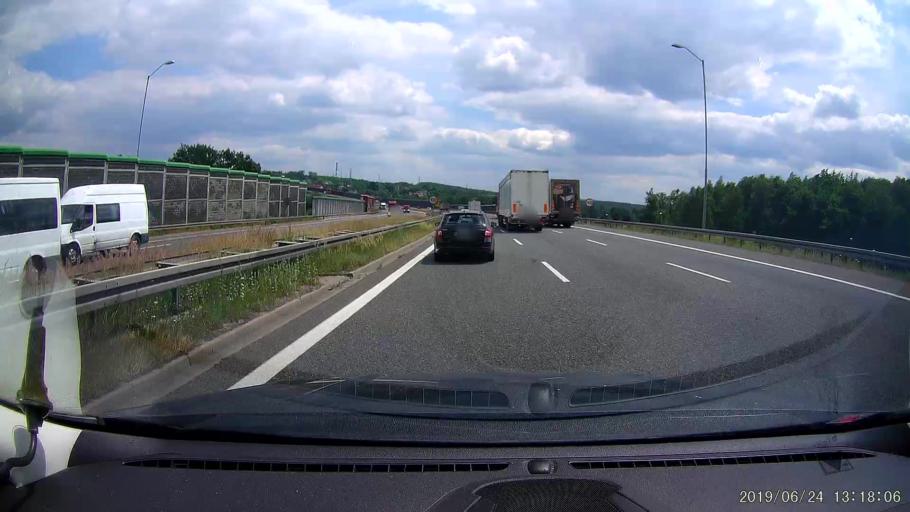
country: PL
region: Silesian Voivodeship
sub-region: Ruda Slaska
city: Ruda Slaska
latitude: 50.2479
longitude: 18.8909
